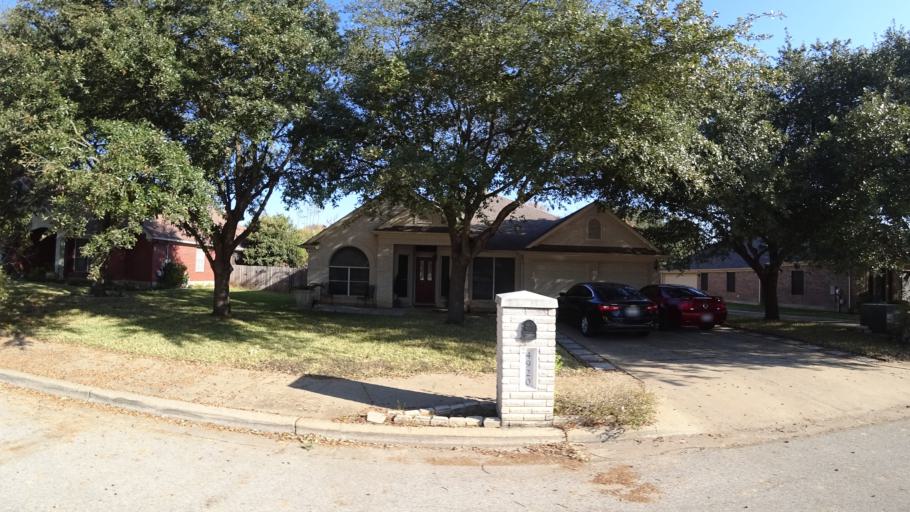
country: US
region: Texas
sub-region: Travis County
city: Shady Hollow
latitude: 30.2185
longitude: -97.8522
